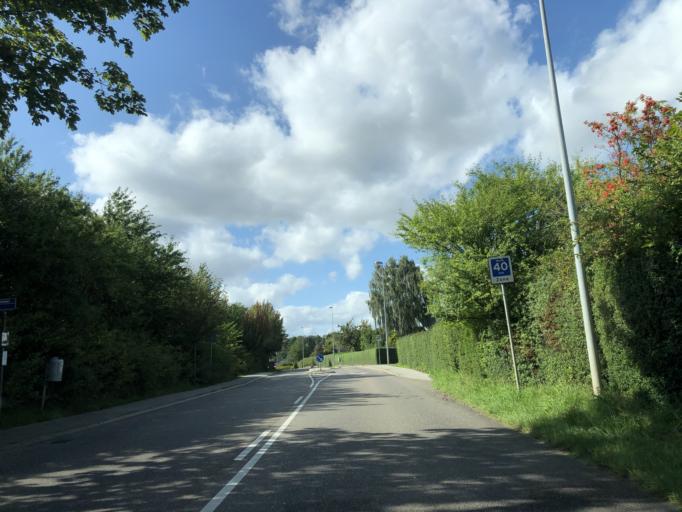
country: DK
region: Central Jutland
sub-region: Skanderborg Kommune
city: Skovby
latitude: 56.1600
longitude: 9.9406
